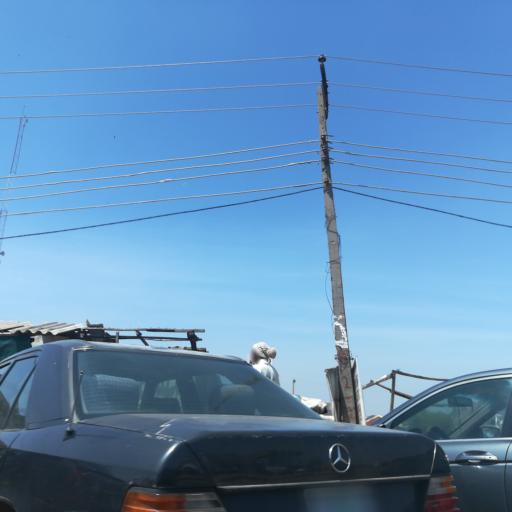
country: NG
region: Plateau
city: Bukuru
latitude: 9.7961
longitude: 8.8661
